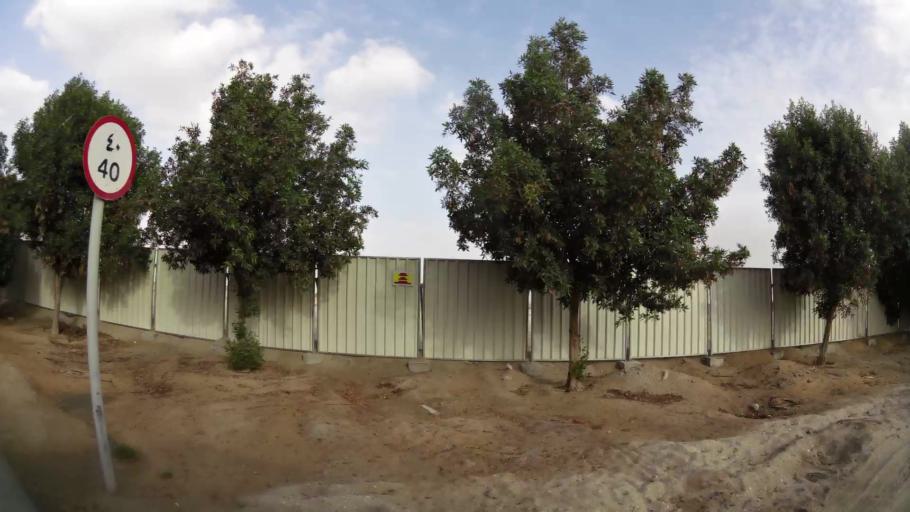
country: AE
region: Abu Dhabi
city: Abu Dhabi
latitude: 24.5001
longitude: 54.6028
